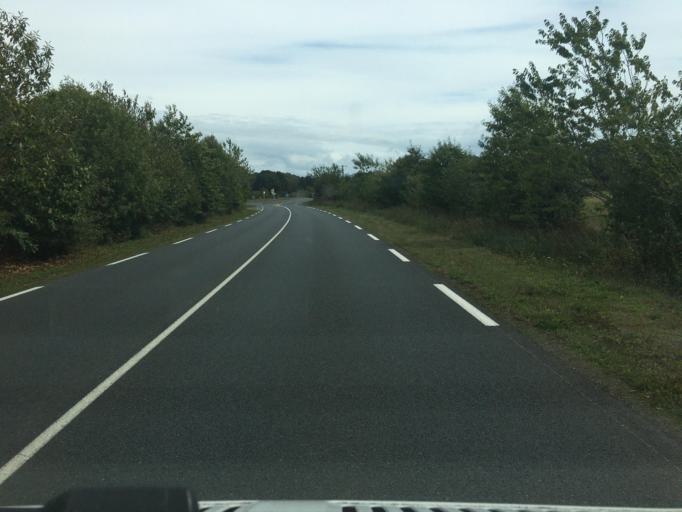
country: FR
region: Brittany
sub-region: Departement du Finistere
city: Plobannalec-Lesconil
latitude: 47.8496
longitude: -4.2178
